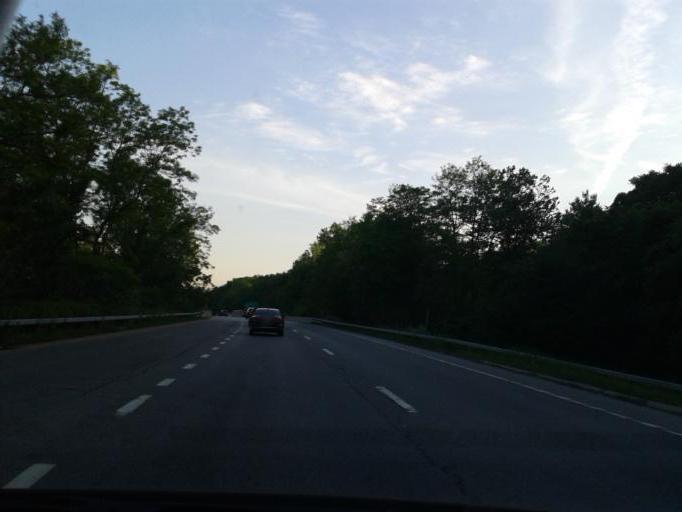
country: US
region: New York
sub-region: Westchester County
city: Harrison
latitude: 40.9923
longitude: -73.7335
